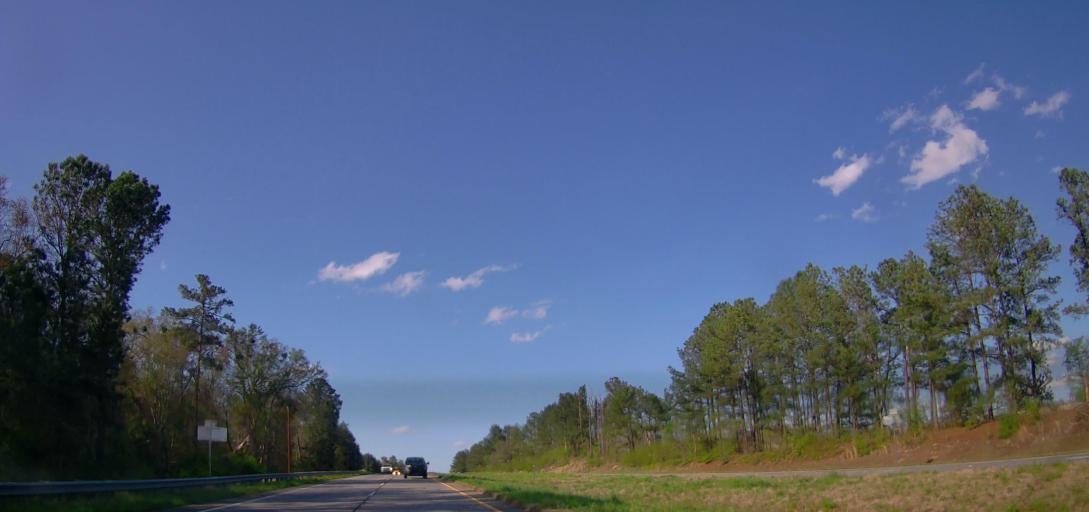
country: US
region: Georgia
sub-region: Baldwin County
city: Hardwick
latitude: 33.0458
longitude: -83.2556
